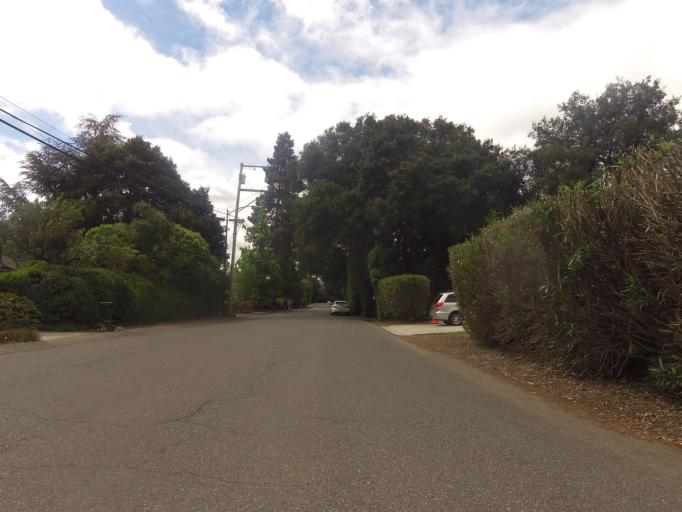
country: US
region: California
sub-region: Santa Clara County
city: Loyola
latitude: 37.3546
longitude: -122.0836
